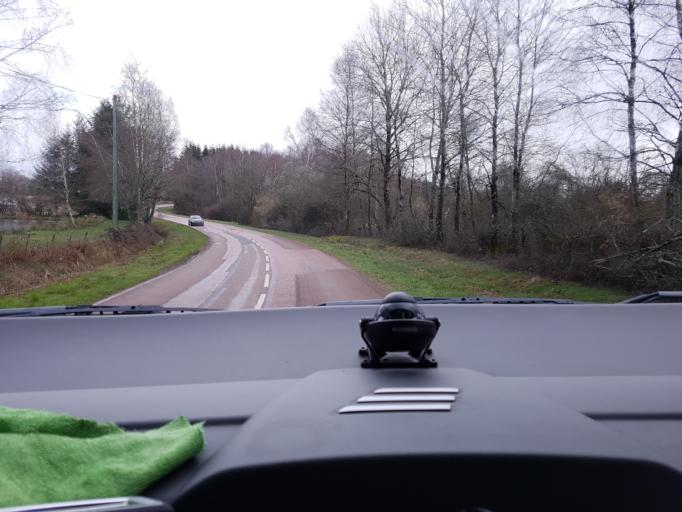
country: FR
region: Bourgogne
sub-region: Departement de la Cote-d'Or
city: Saulieu
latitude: 47.2750
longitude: 4.0239
